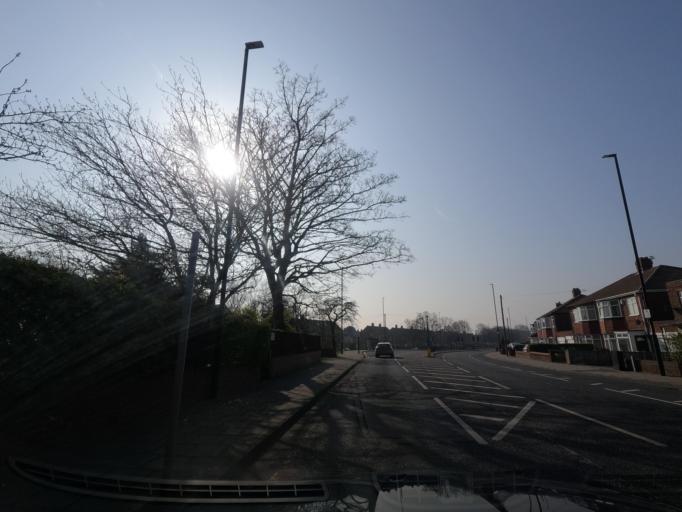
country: GB
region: England
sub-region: Newcastle upon Tyne
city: Gosforth
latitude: 55.0055
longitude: -1.5773
